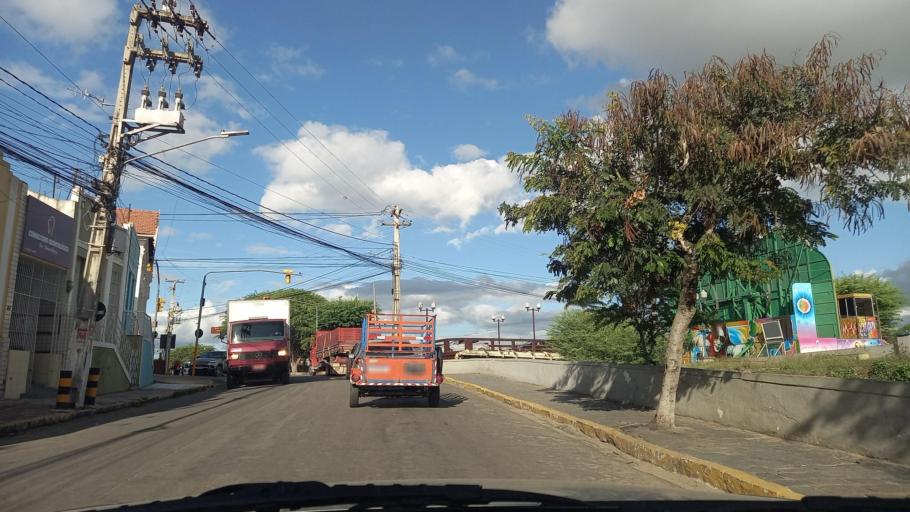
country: BR
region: Pernambuco
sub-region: Gravata
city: Gravata
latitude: -8.2047
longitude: -35.5710
